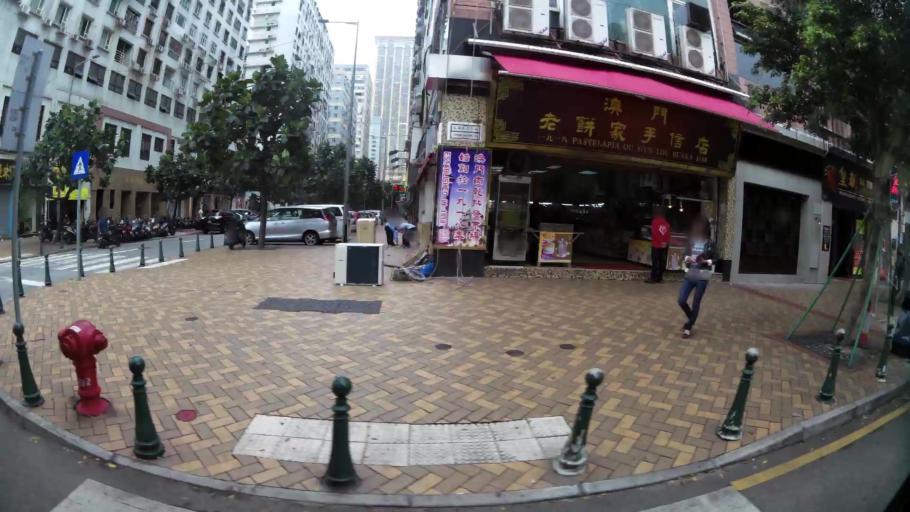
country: MO
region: Macau
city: Macau
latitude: 22.1905
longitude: 113.5535
